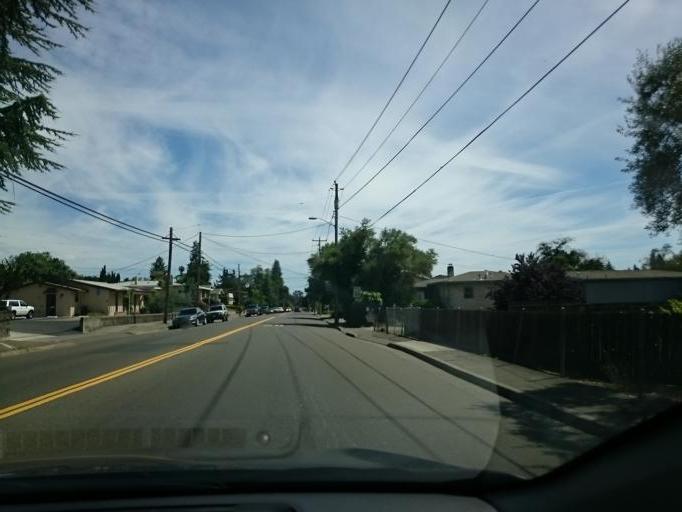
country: US
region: California
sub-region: Sonoma County
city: Healdsburg
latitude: 38.6200
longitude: -122.8720
